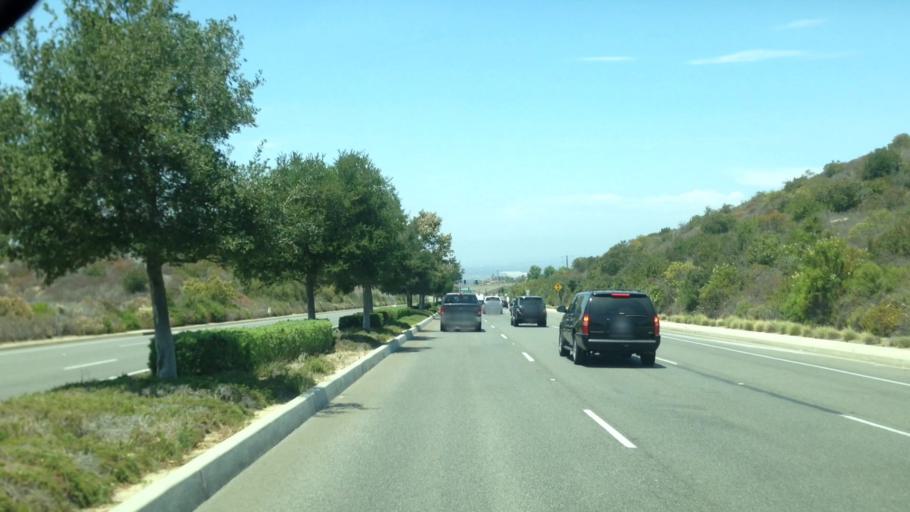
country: US
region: California
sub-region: Orange County
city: San Joaquin Hills
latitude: 33.6123
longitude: -117.8258
